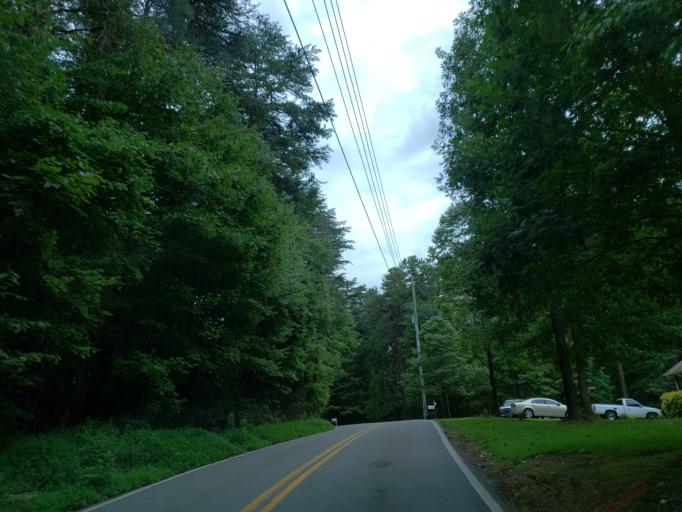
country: US
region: Georgia
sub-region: Pickens County
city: Jasper
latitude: 34.4241
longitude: -84.5413
